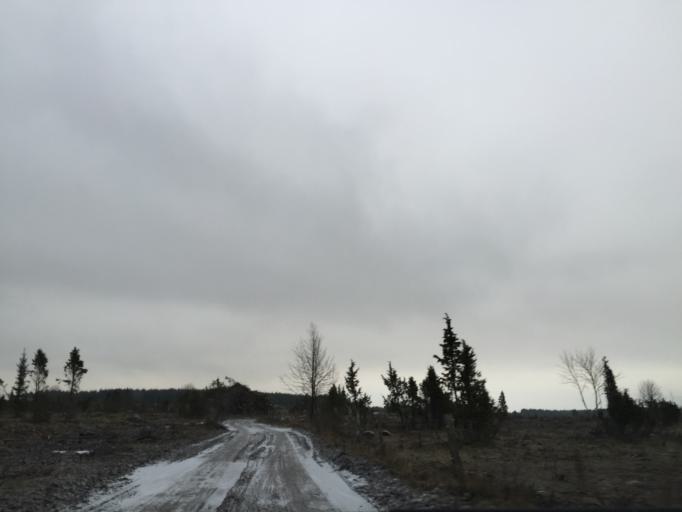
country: EE
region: Saare
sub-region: Orissaare vald
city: Orissaare
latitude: 58.6127
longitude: 23.0853
